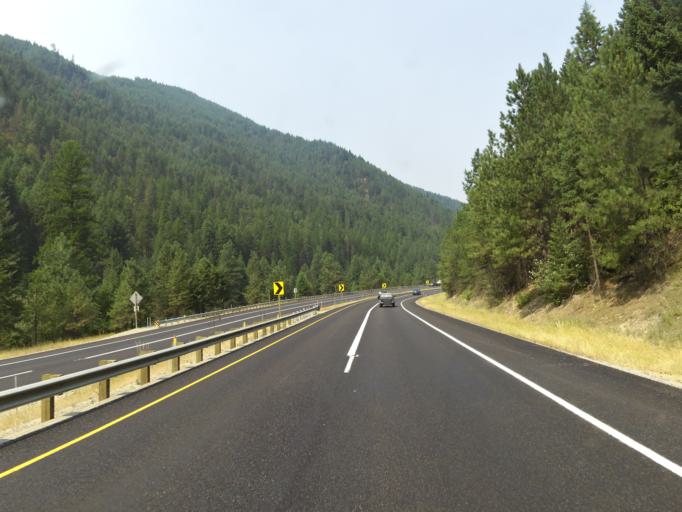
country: US
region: Montana
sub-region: Sanders County
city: Thompson Falls
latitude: 47.3160
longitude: -115.2407
